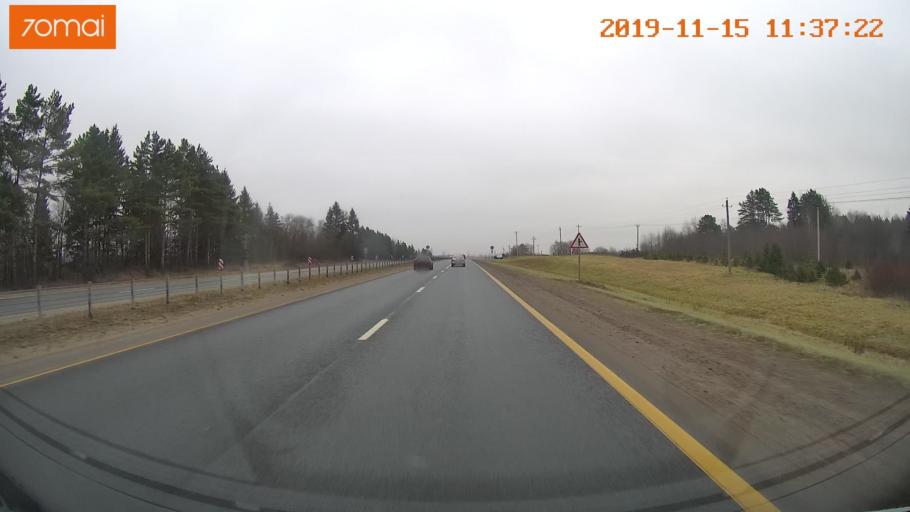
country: RU
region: Vologda
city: Molochnoye
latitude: 59.2053
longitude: 39.6711
